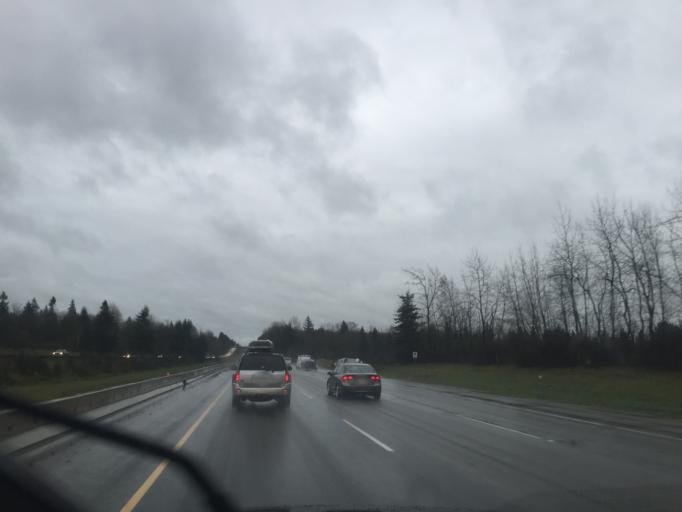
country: CA
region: British Columbia
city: Langley
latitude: 49.1250
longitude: -122.5528
